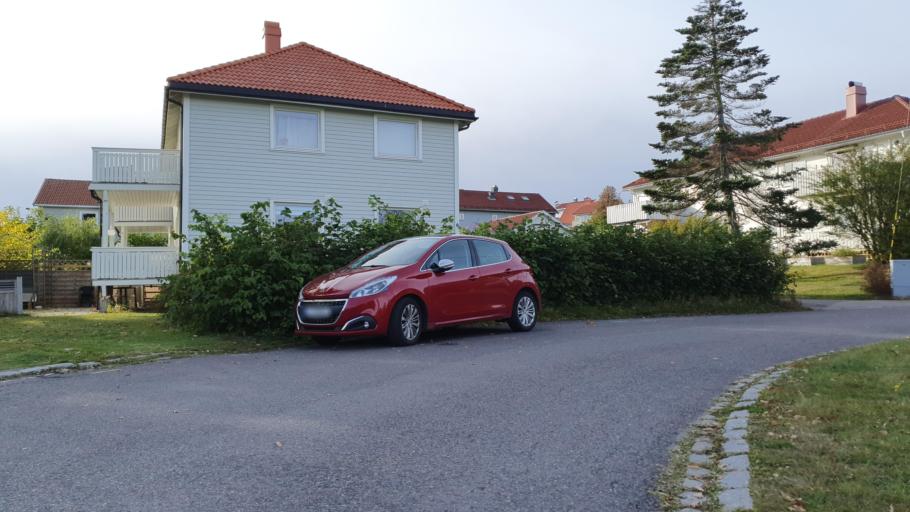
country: NO
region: Vestfold
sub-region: Tonsberg
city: Tonsberg
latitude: 59.2777
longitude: 10.4218
